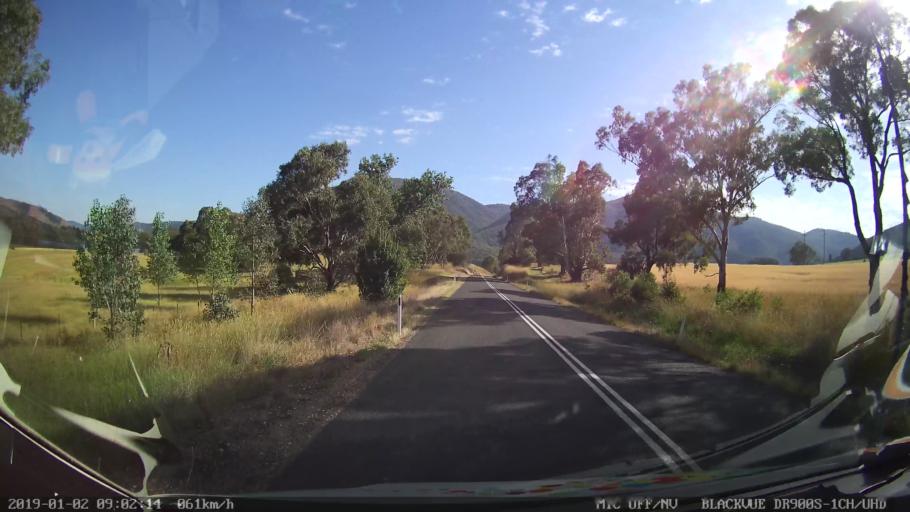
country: AU
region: New South Wales
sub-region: Tumut Shire
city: Tumut
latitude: -35.5746
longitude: 148.3113
